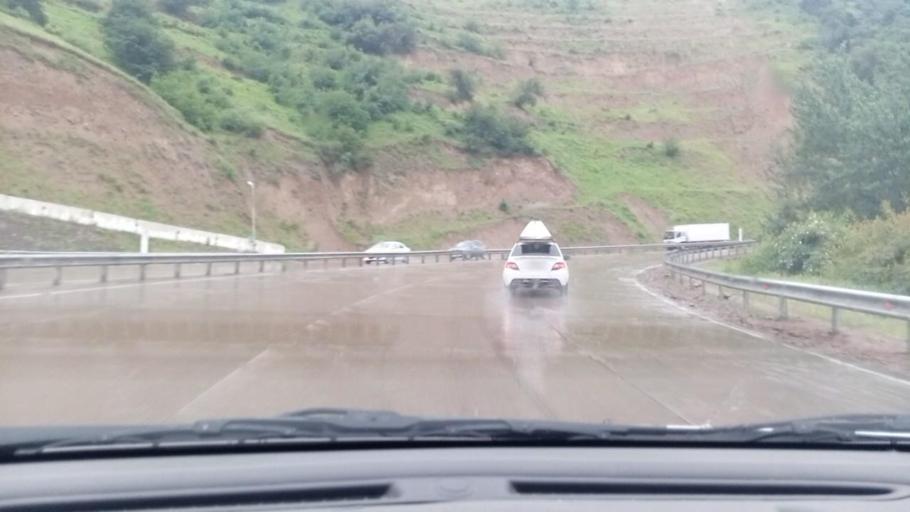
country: UZ
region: Toshkent
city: Angren
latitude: 41.1550
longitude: 70.4480
